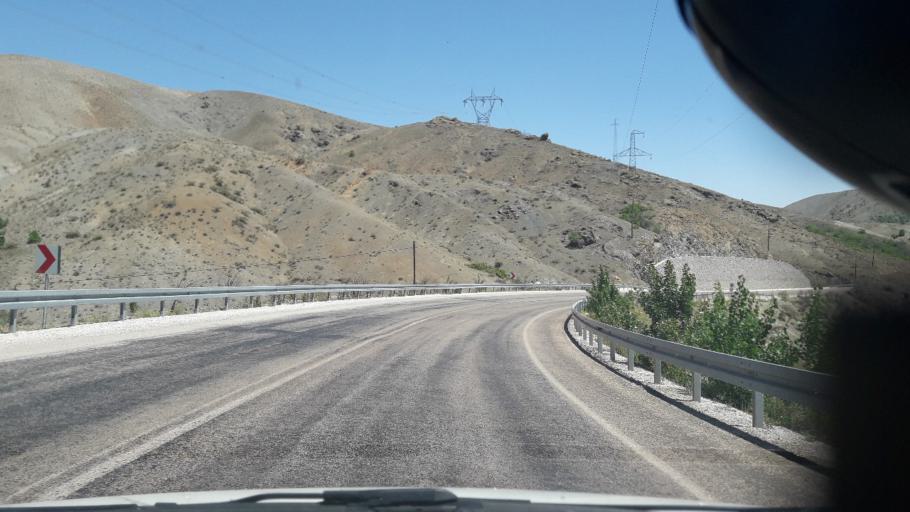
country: TR
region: Malatya
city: Hekimhan
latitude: 38.8348
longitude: 37.8486
